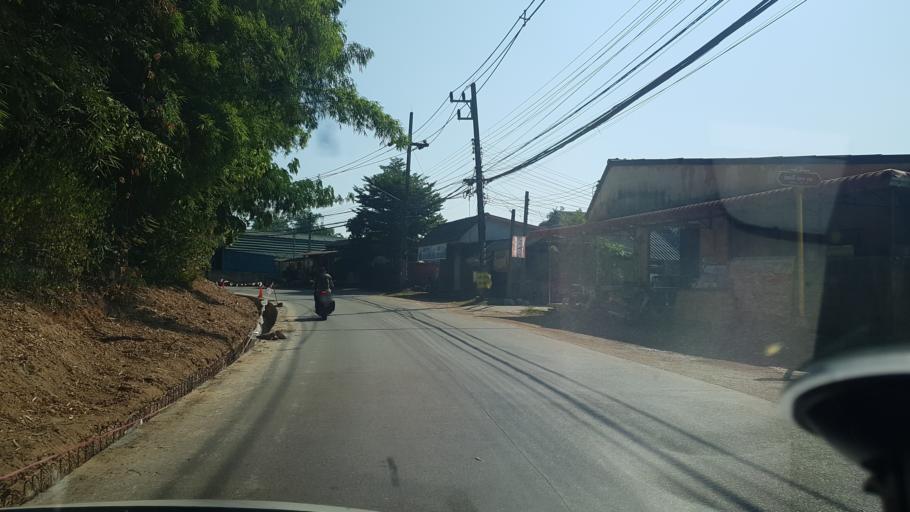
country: TH
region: Chiang Rai
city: Chiang Rai
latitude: 19.9067
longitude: 99.8013
